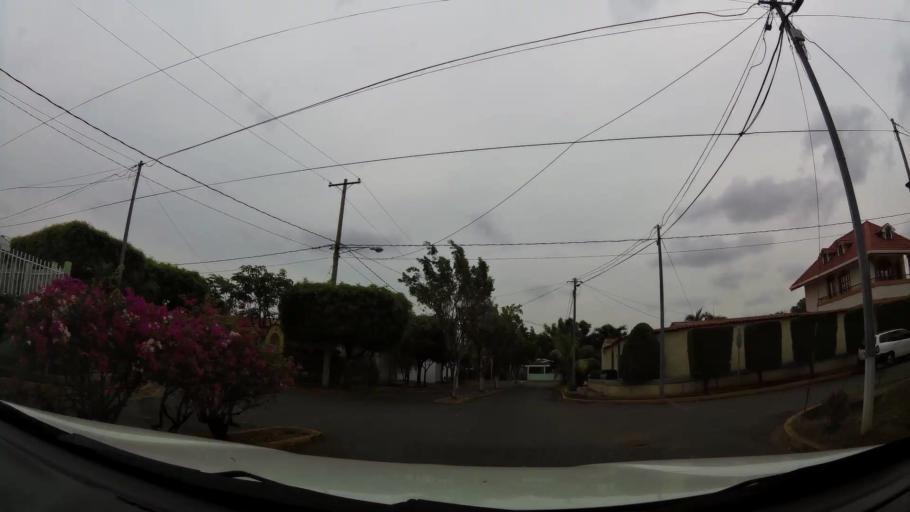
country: NI
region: Masaya
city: Ticuantepe
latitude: 12.0635
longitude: -86.1848
